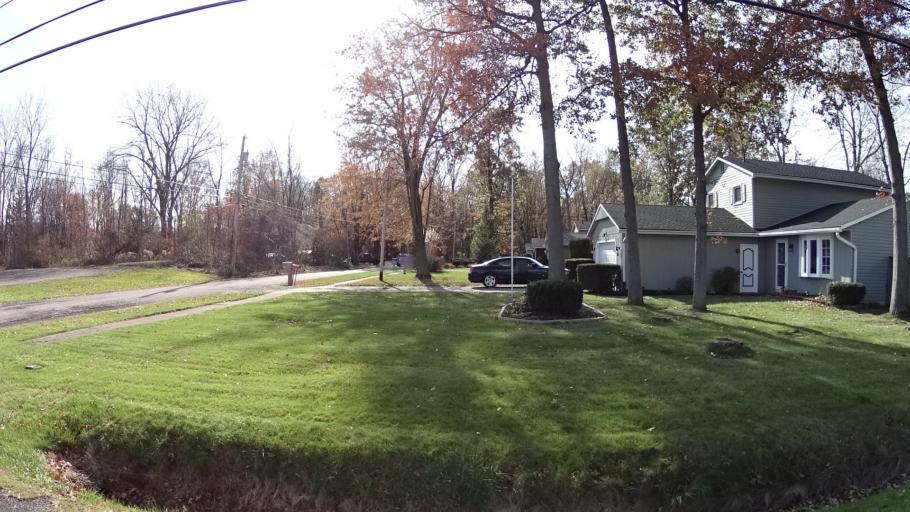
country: US
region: Ohio
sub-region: Lorain County
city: Sheffield Lake
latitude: 41.4901
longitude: -82.0910
